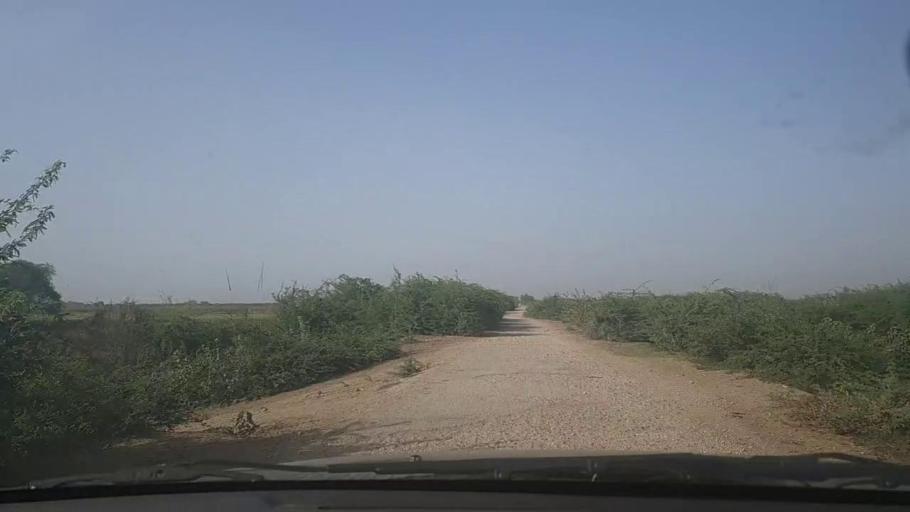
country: PK
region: Sindh
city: Keti Bandar
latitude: 24.2547
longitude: 67.5626
